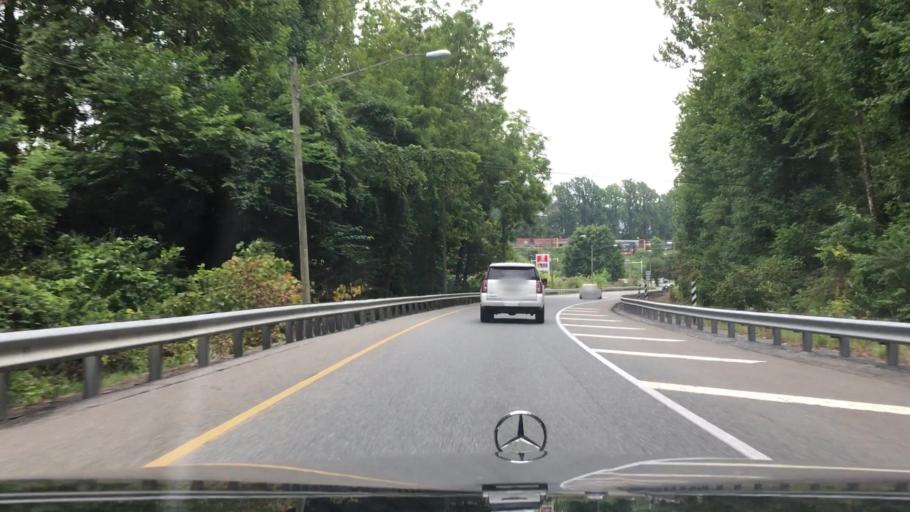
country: US
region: Virginia
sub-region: City of Lynchburg
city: West Lynchburg
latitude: 37.3607
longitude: -79.1822
